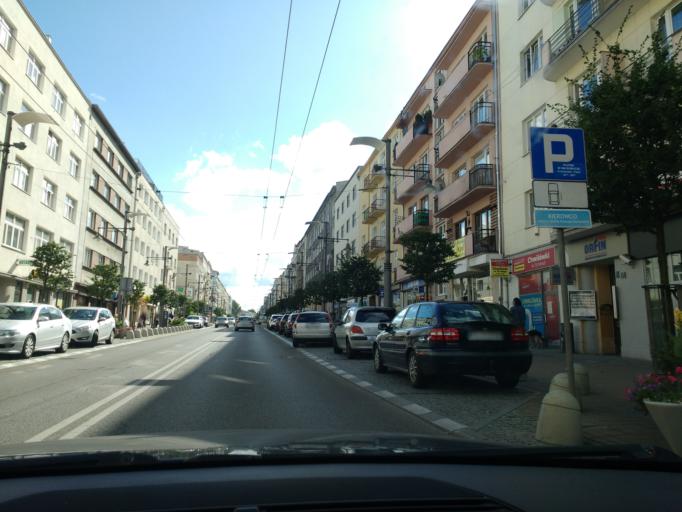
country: PL
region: Pomeranian Voivodeship
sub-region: Gdynia
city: Gdynia
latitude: 54.5134
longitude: 18.5399
